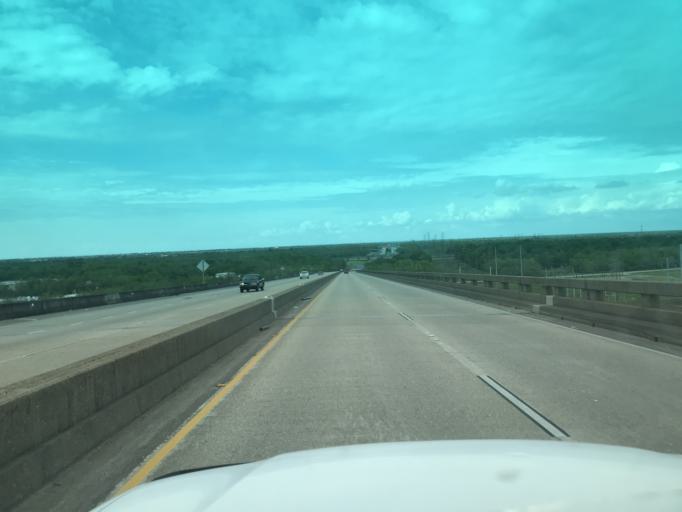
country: US
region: Louisiana
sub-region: Saint Bernard Parish
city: Chalmette
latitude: 30.0081
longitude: -89.9393
